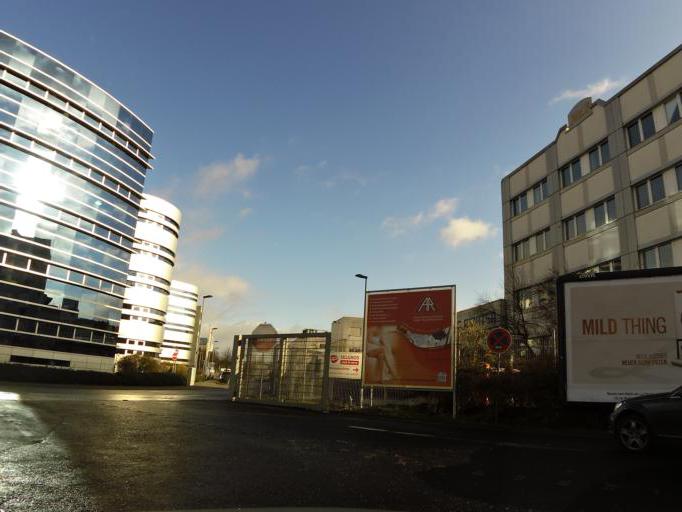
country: DE
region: Hesse
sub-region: Regierungsbezirk Darmstadt
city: Neu Isenburg
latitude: 50.0476
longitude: 8.7105
